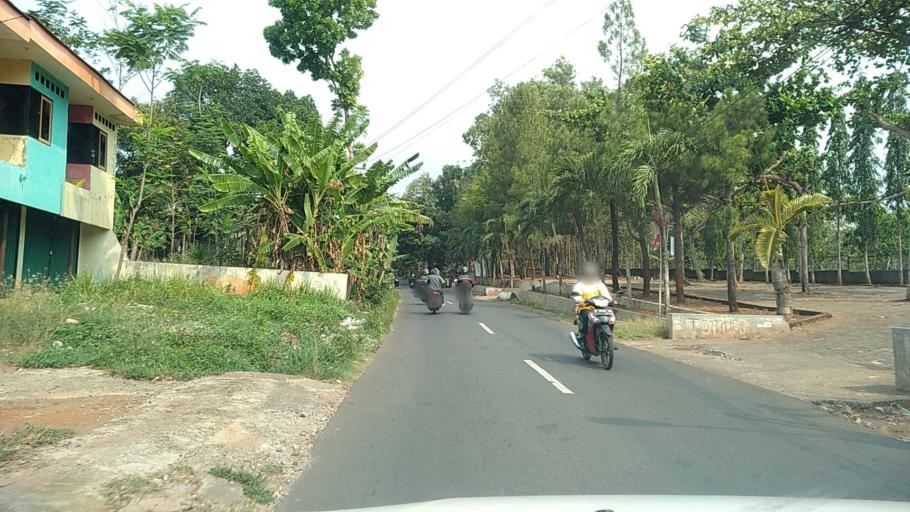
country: ID
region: Central Java
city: Semarang
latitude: -7.0119
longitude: 110.3308
